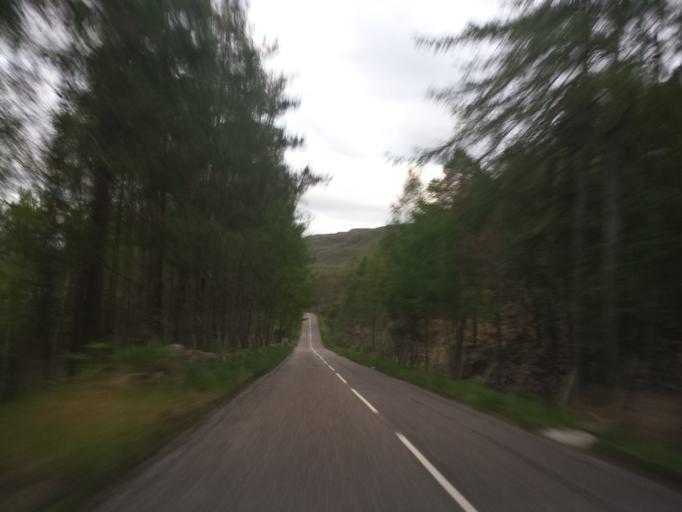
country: GB
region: Scotland
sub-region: Highland
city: Ullapool
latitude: 57.5276
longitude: -5.5396
